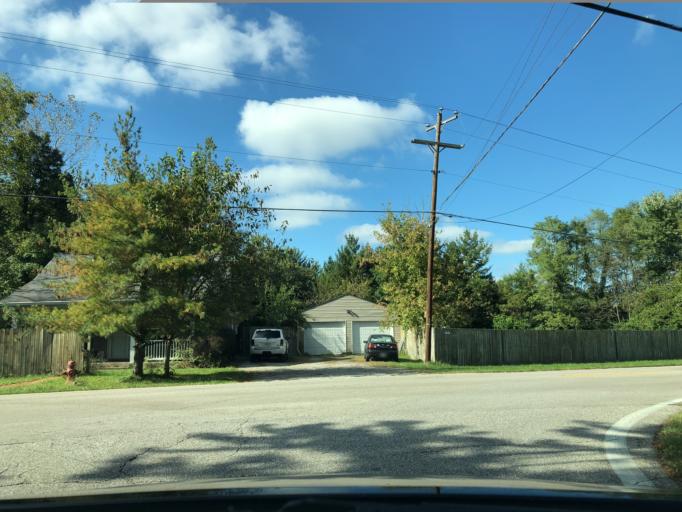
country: US
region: Ohio
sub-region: Hamilton County
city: Loveland
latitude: 39.2489
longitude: -84.2528
